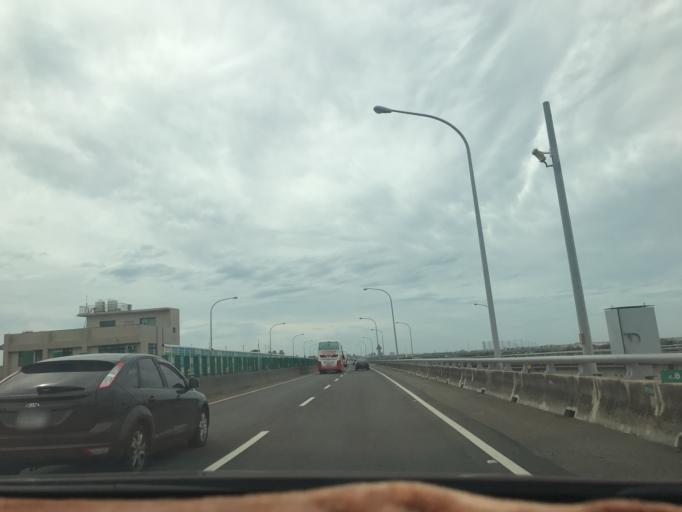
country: TW
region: Taiwan
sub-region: Hsinchu
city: Zhubei
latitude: 24.8204
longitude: 120.9936
